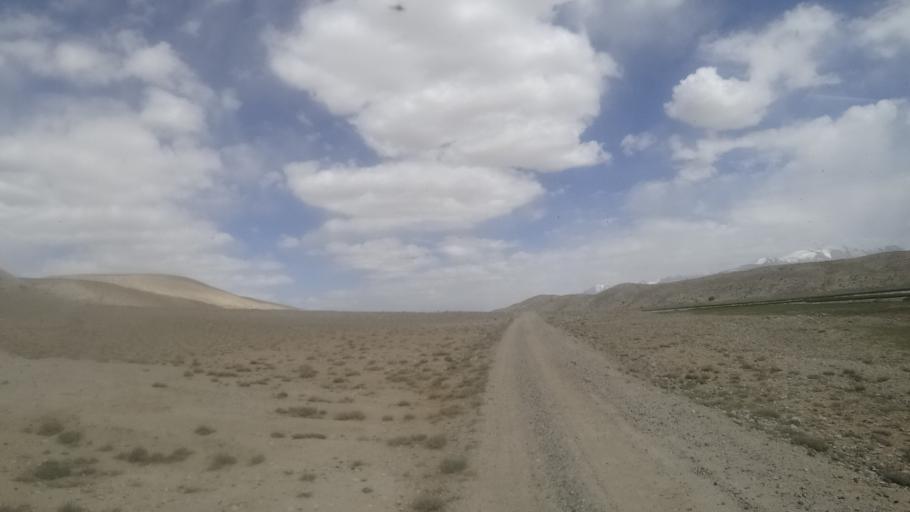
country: AF
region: Badakhshan
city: Khandud
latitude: 37.4088
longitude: 73.1570
